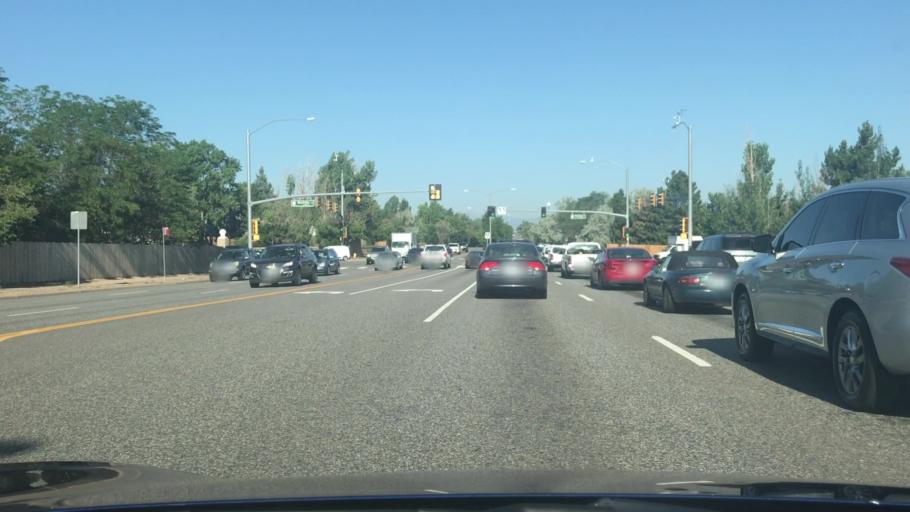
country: US
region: Colorado
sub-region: Arapahoe County
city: Dove Valley
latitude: 39.6531
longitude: -104.7902
